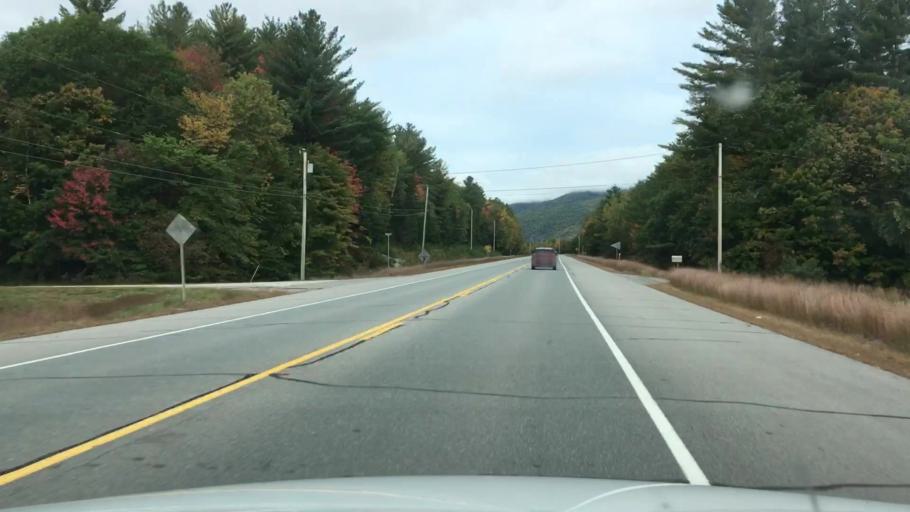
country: US
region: New Hampshire
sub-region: Coos County
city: Gorham
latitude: 44.3946
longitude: -71.0517
